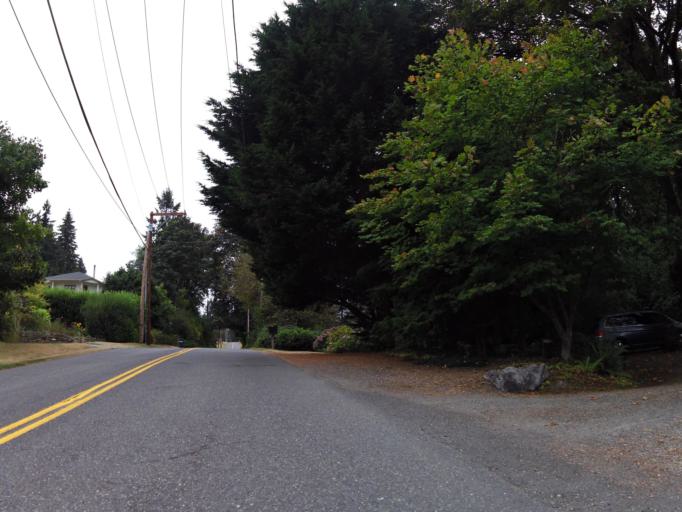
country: US
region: Washington
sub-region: Kitsap County
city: Lofall
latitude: 47.8109
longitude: -122.6599
